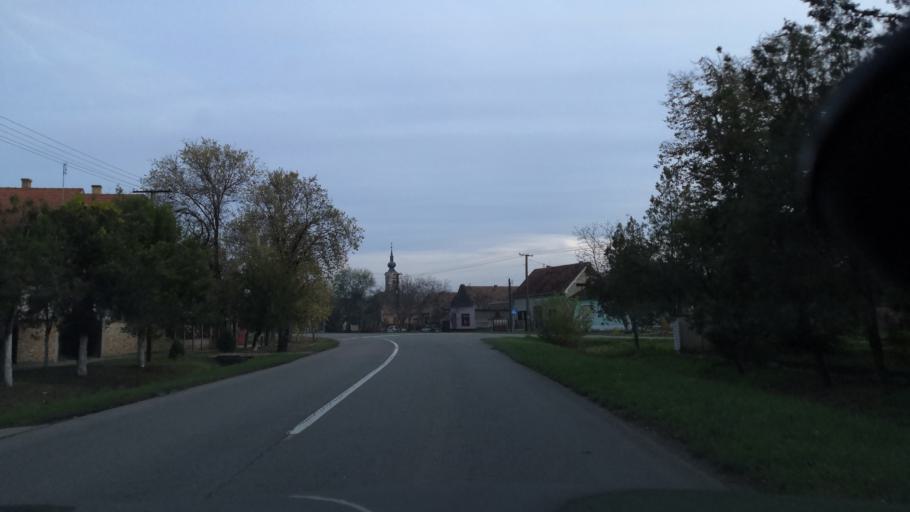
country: RS
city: Ostojicevo
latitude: 45.8910
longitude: 20.1641
